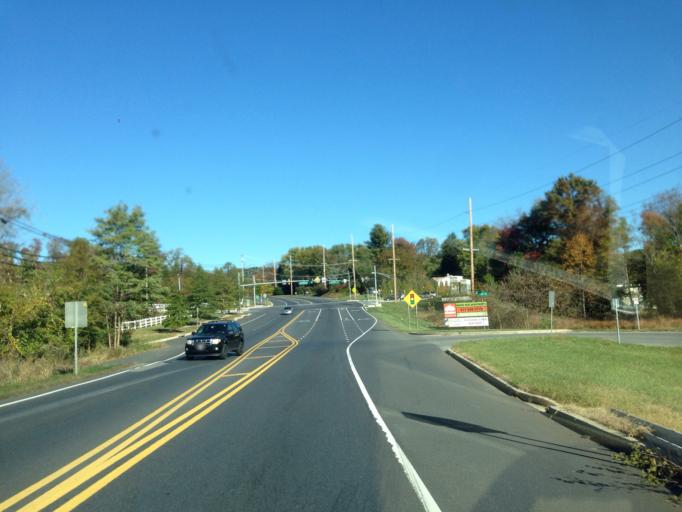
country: US
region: Maryland
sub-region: Montgomery County
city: Clarksburg
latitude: 39.2218
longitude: -77.2598
